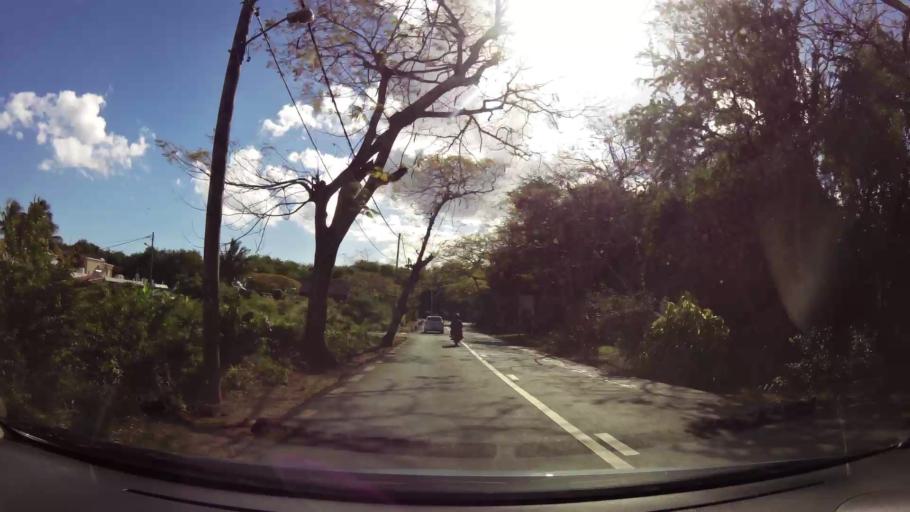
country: MU
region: Black River
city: Albion
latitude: -20.2131
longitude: 57.4066
